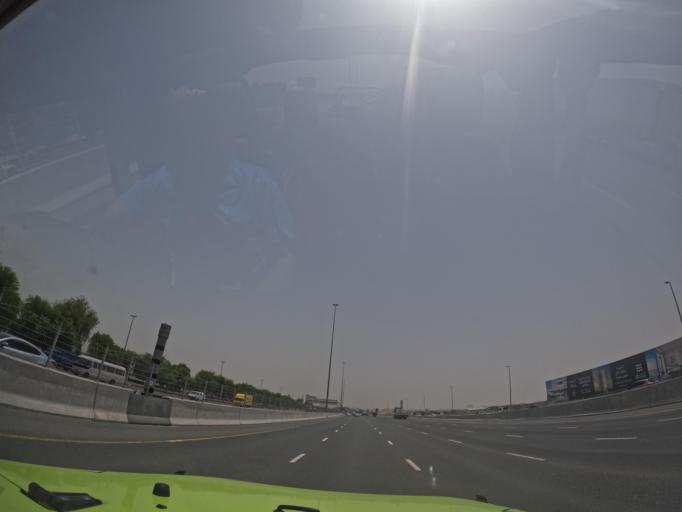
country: AE
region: Ash Shariqah
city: Sharjah
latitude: 25.1290
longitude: 55.3770
